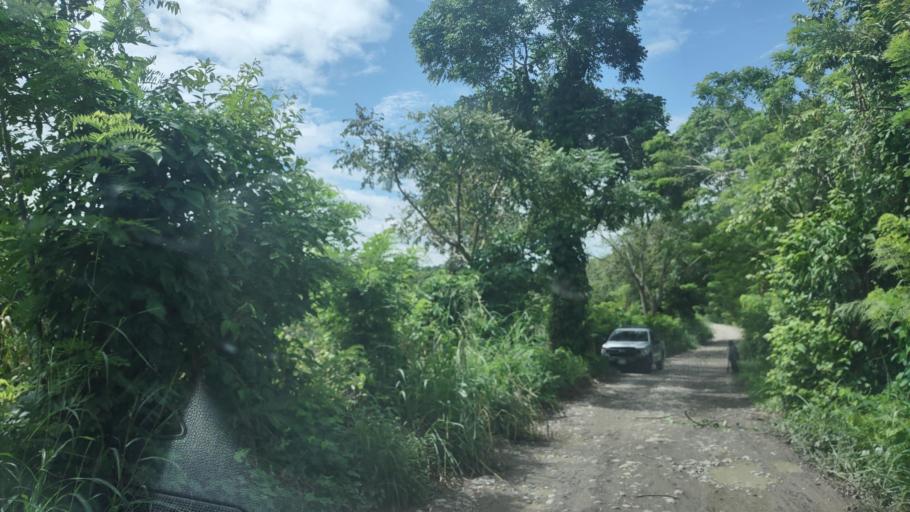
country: MX
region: Veracruz
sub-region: Atzalan
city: Colonias Pedernales
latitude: 20.0567
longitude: -97.0123
